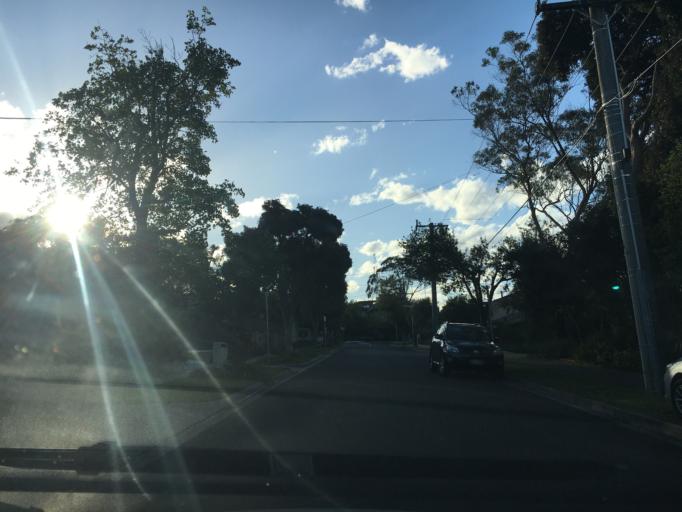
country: AU
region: Victoria
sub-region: Whitehorse
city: Vermont South
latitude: -37.8808
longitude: 145.1716
